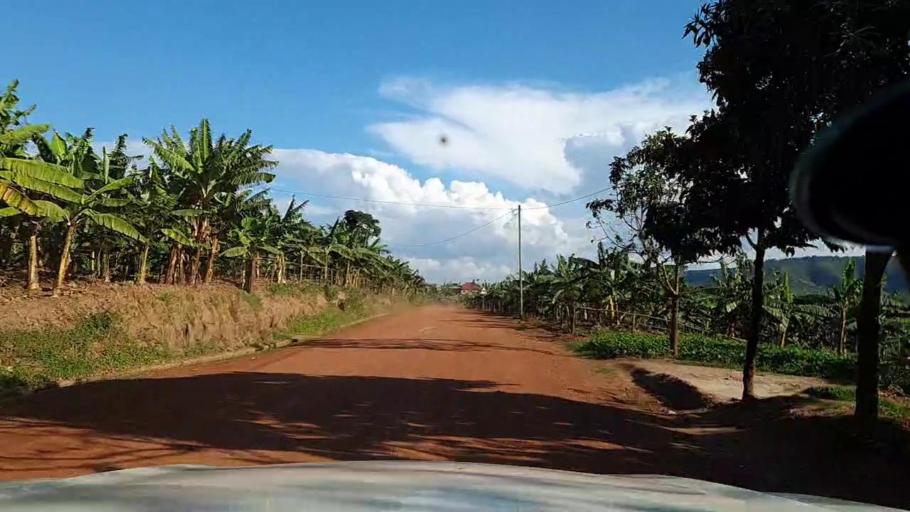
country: RW
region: Kigali
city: Kigali
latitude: -1.8605
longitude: 29.9184
